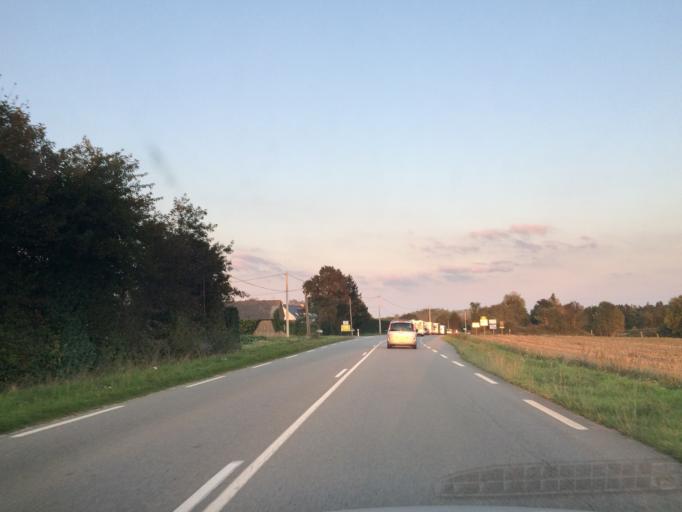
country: FR
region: Pays de la Loire
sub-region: Departement de la Loire-Atlantique
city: Port-Saint-Pere
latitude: 47.1340
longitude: -1.7678
